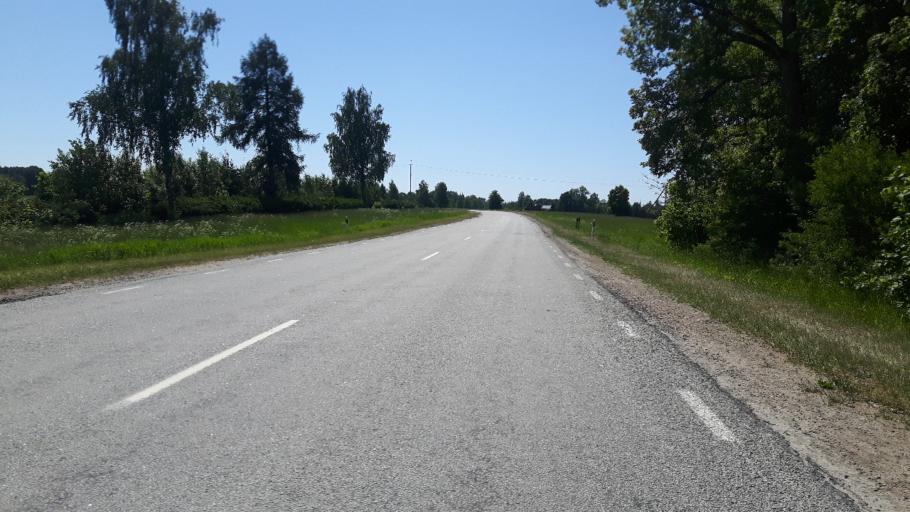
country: EE
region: Paernumaa
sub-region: Sindi linn
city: Sindi
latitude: 58.4366
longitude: 24.7371
